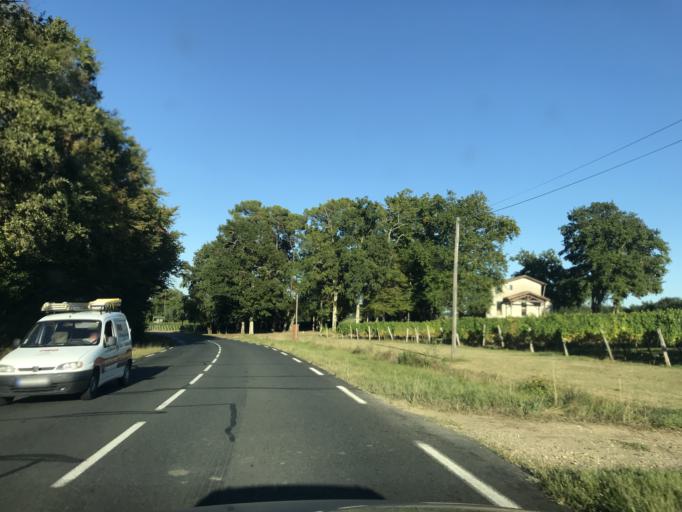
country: FR
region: Aquitaine
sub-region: Departement de la Gironde
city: Sauveterre-de-Guyenne
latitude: 44.6507
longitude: -0.1174
